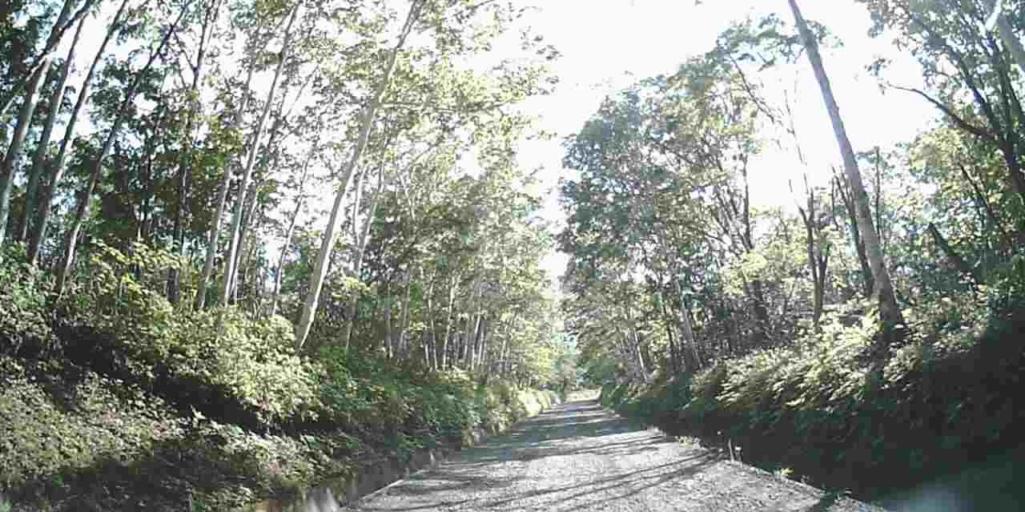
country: JP
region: Hokkaido
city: Shiraoi
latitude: 42.7035
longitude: 141.3938
